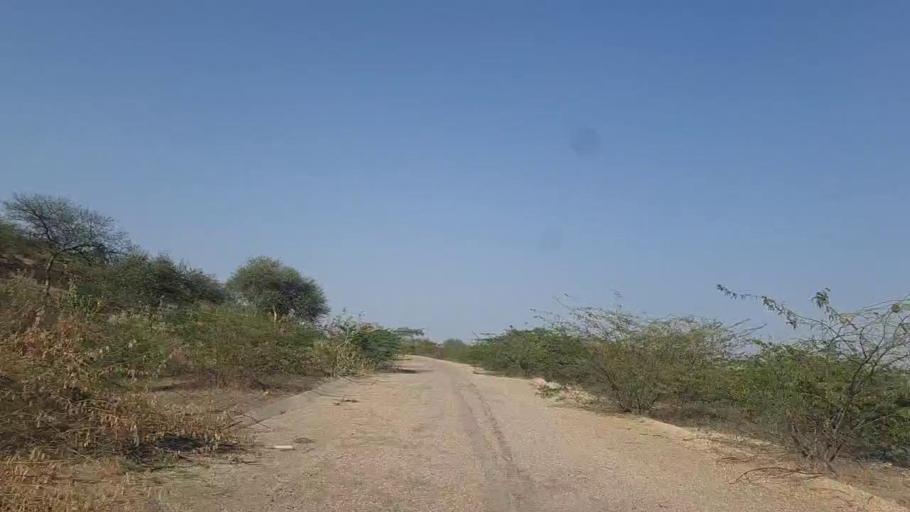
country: PK
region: Sindh
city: Naukot
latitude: 24.6152
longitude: 69.3468
